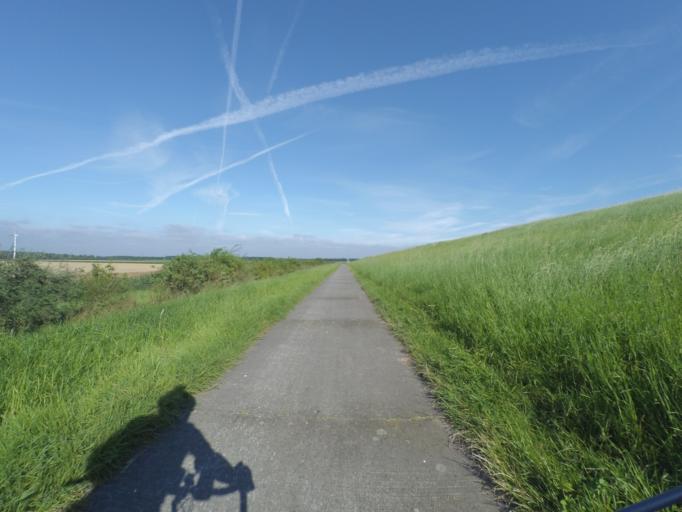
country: NL
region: Flevoland
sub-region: Gemeente Lelystad
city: Lelystad
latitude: 52.4353
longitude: 5.4495
